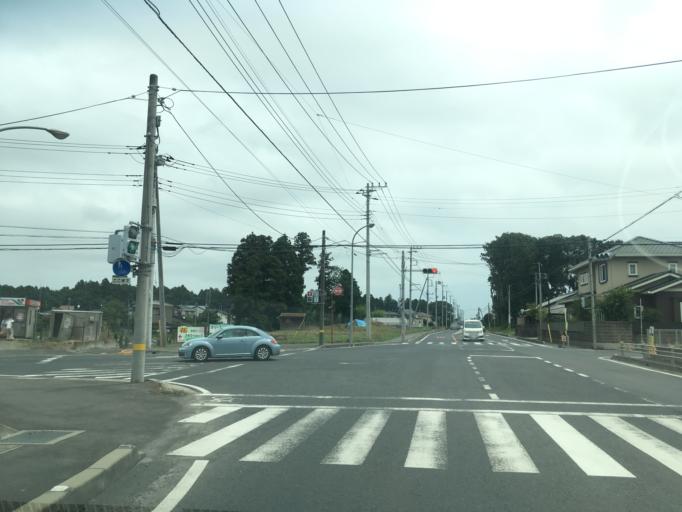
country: JP
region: Ibaraki
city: Katsuta
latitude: 36.3829
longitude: 140.5467
